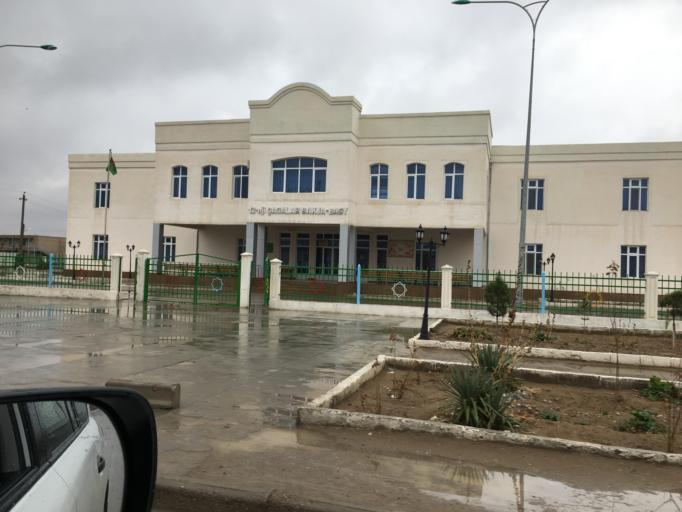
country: TM
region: Mary
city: Yoloeten
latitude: 37.2923
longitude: 62.3689
